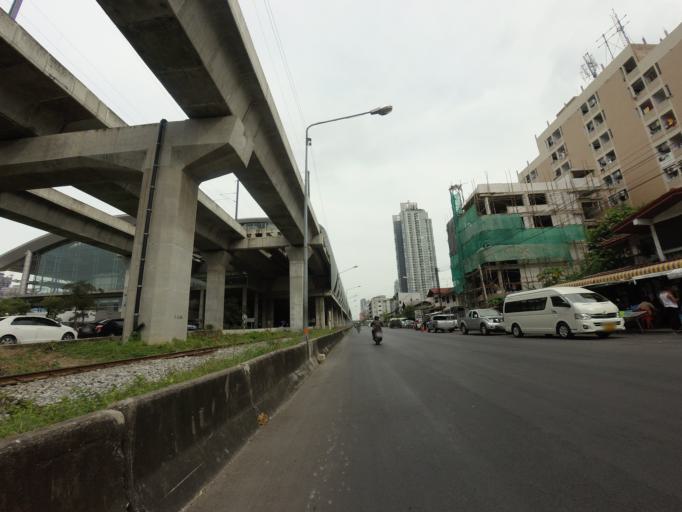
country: TH
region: Bangkok
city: Din Daeng
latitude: 13.7512
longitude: 100.5589
